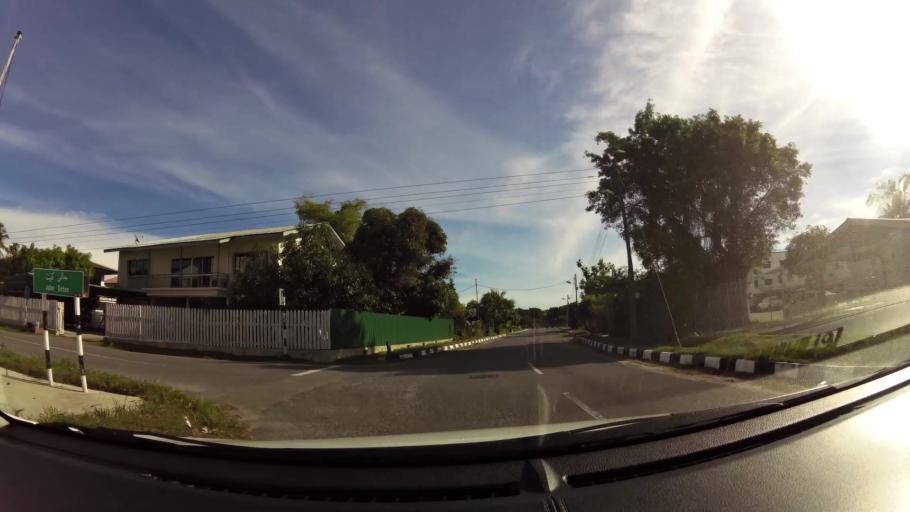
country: BN
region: Belait
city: Kuala Belait
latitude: 4.5842
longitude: 114.1893
